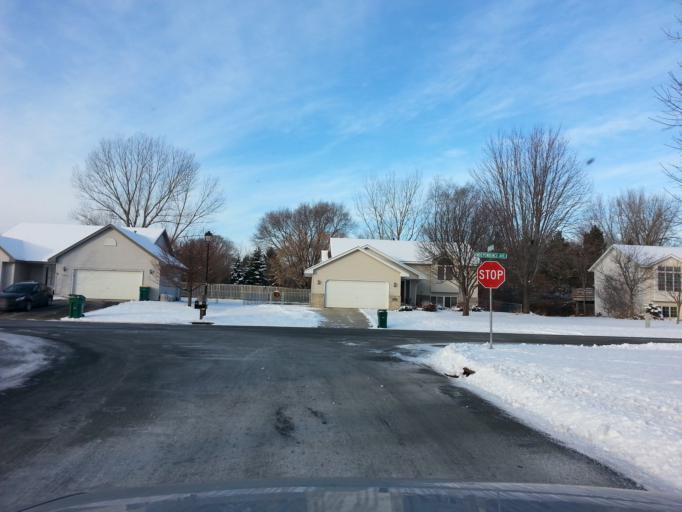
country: US
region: Minnesota
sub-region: Scott County
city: Savage
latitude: 44.7741
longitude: -93.3978
